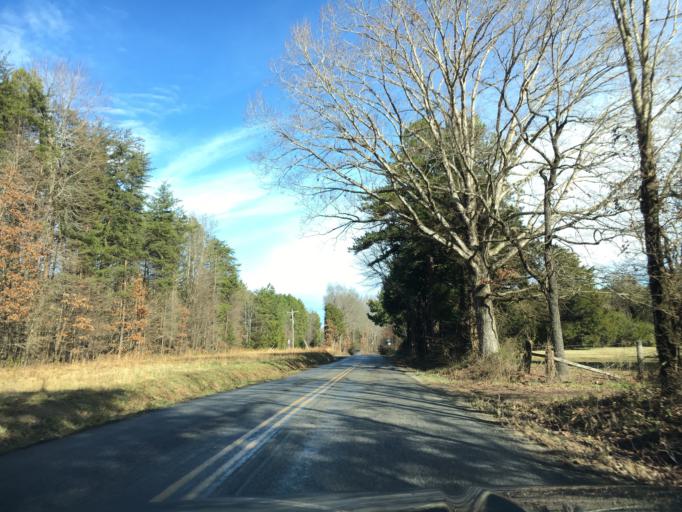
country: US
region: Virginia
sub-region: Cumberland County
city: Cumberland
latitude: 37.3453
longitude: -78.1590
